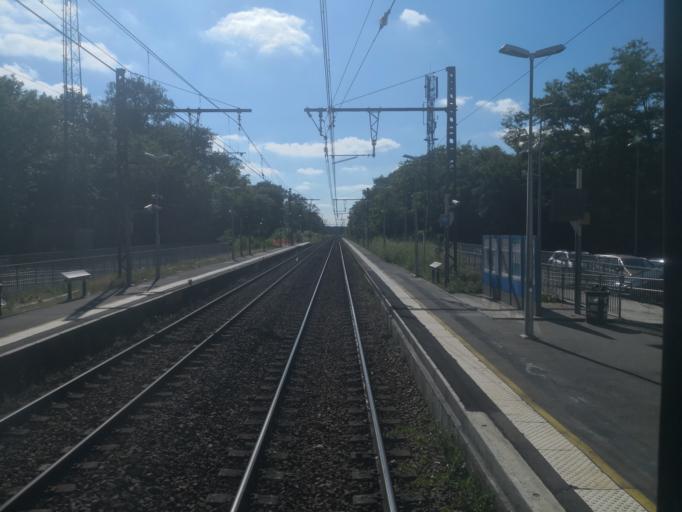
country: FR
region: Ile-de-France
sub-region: Departement de Seine-et-Marne
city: Thomery
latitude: 48.3943
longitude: 2.7636
